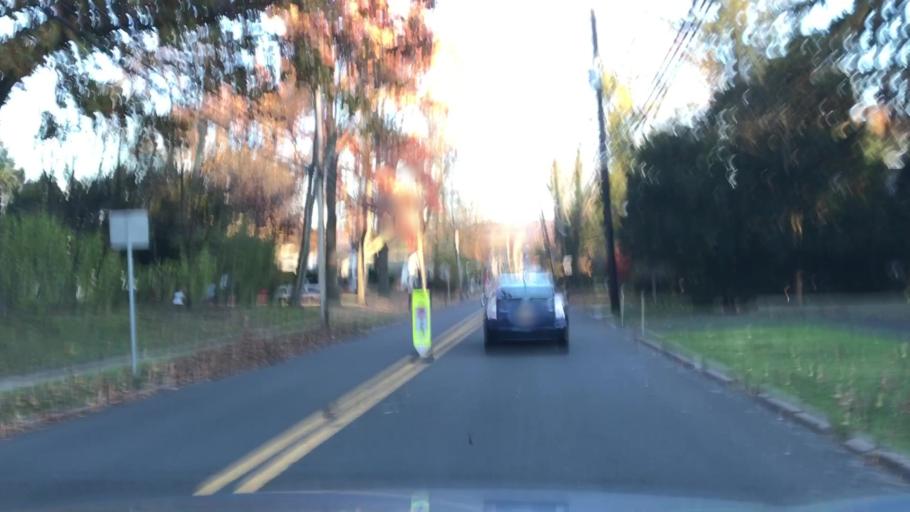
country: US
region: New Jersey
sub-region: Bergen County
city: Norwood
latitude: 40.9975
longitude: -73.9597
